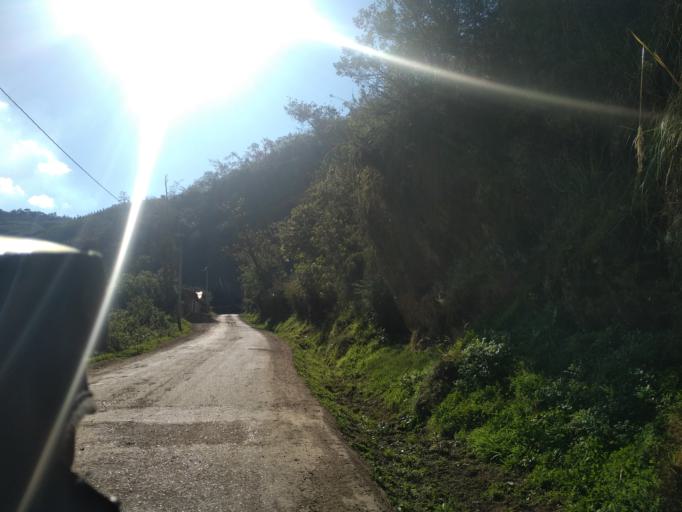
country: PE
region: Amazonas
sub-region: Provincia de Chachapoyas
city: Montevideo
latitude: -6.7264
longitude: -77.8284
